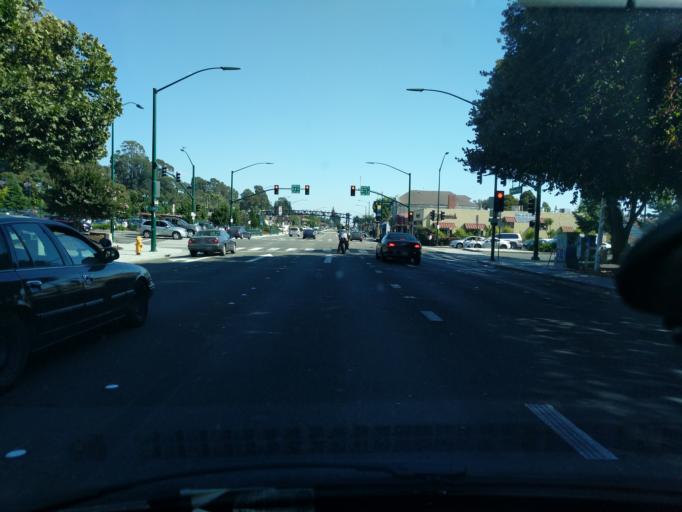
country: US
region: California
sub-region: Alameda County
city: Hayward
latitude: 37.6703
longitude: -122.0823
